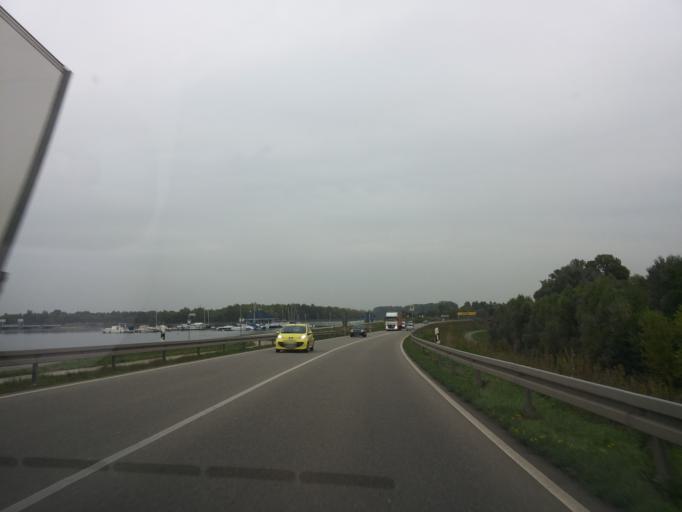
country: FR
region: Alsace
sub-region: Departement du Bas-Rhin
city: Plobsheim
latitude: 48.4929
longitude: 7.7771
